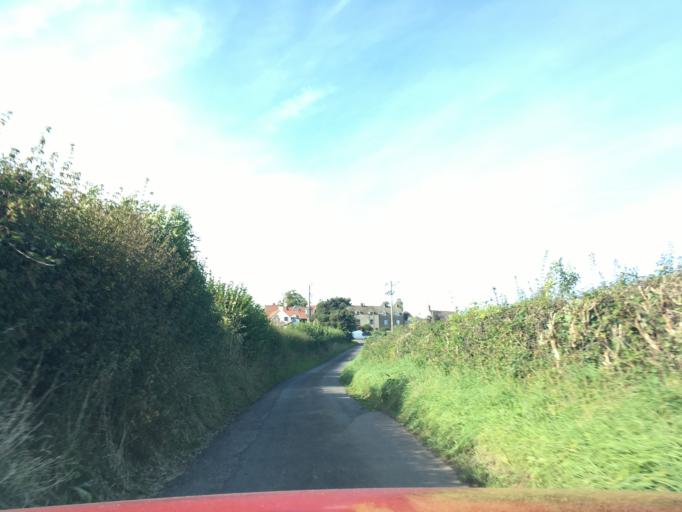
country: GB
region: England
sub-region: South Gloucestershire
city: Charfield
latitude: 51.6159
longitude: -2.4342
